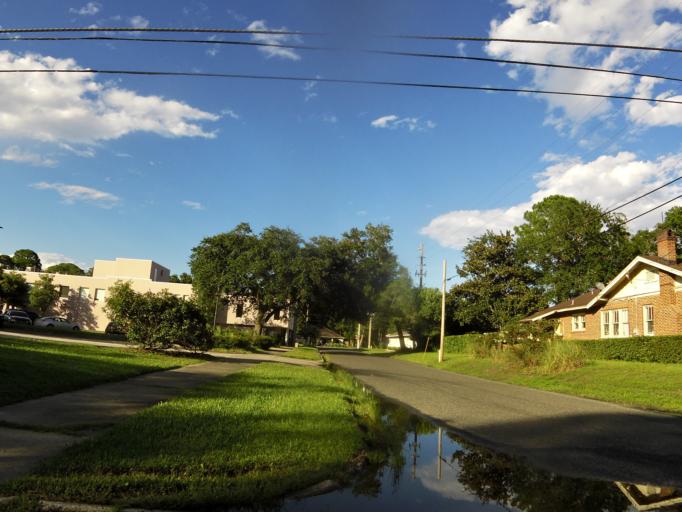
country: US
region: Florida
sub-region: Duval County
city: Jacksonville
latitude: 30.3128
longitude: -81.7204
